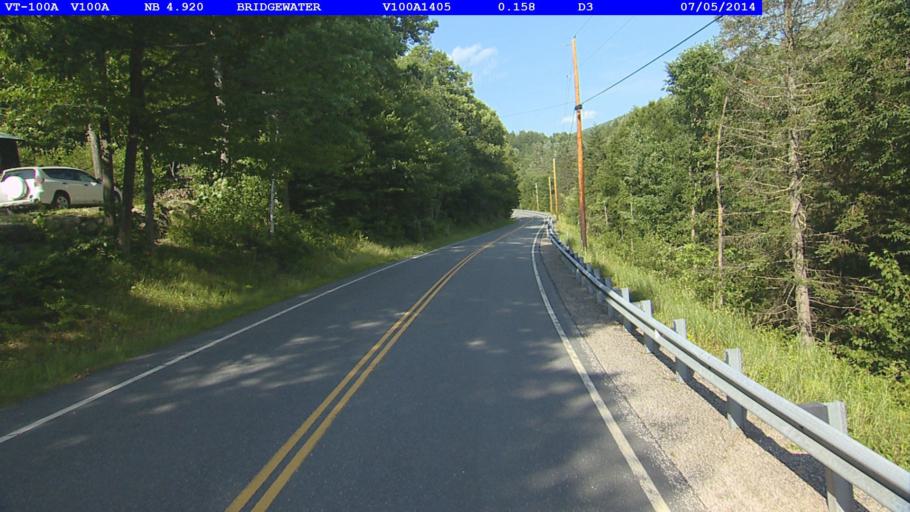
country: US
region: Vermont
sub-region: Windsor County
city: Woodstock
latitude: 43.5708
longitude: -72.6785
